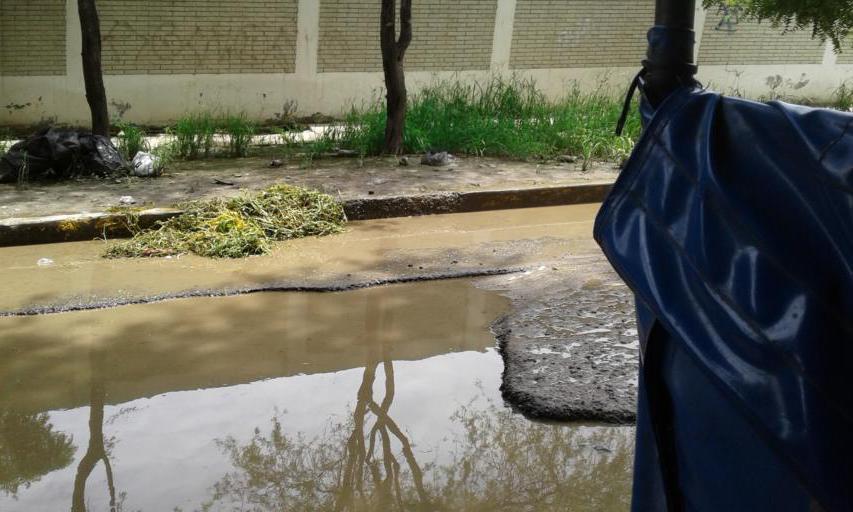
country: PE
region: Piura
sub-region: Provincia de Piura
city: Piura
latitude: -5.1962
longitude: -80.6331
